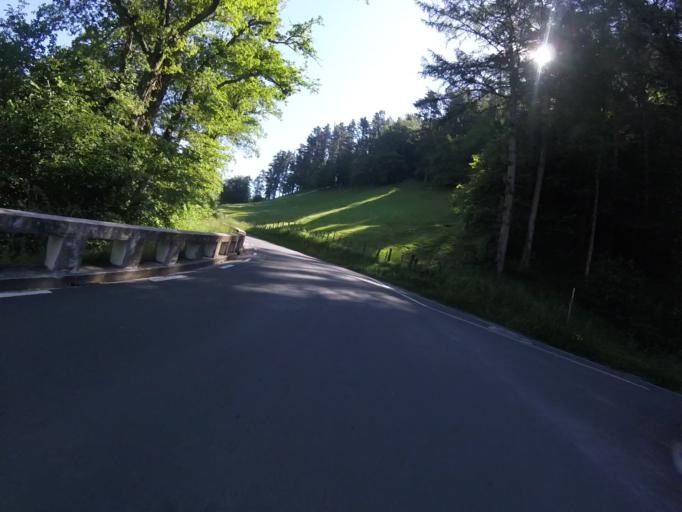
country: ES
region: Basque Country
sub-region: Provincia de Guipuzcoa
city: Albiztur
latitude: 43.1195
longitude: -2.1555
